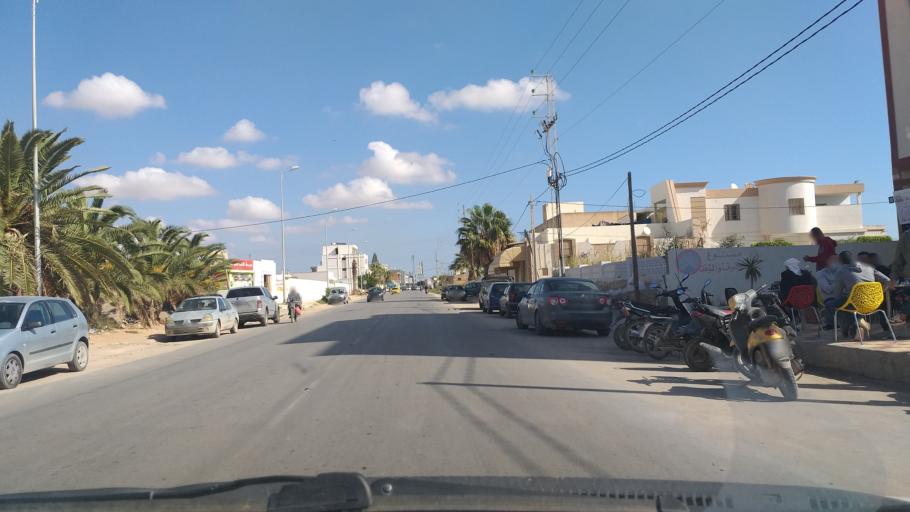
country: TN
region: Safaqis
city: Al Qarmadah
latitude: 34.7914
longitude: 10.8057
